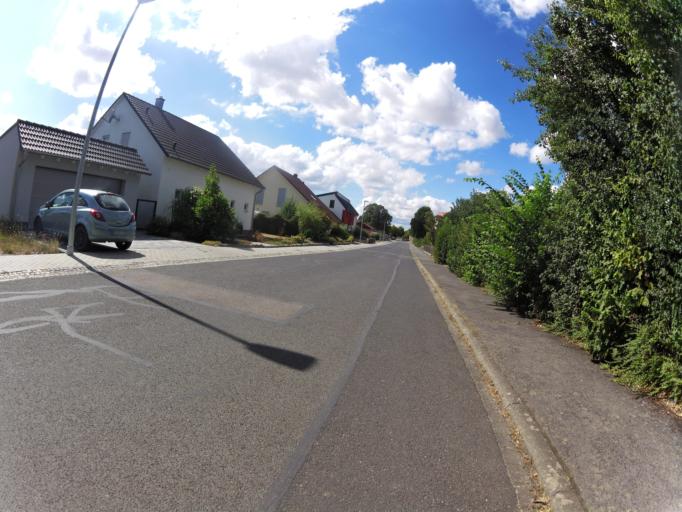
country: DE
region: Bavaria
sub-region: Regierungsbezirk Unterfranken
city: Sonderhofen
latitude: 49.5717
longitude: 10.0167
